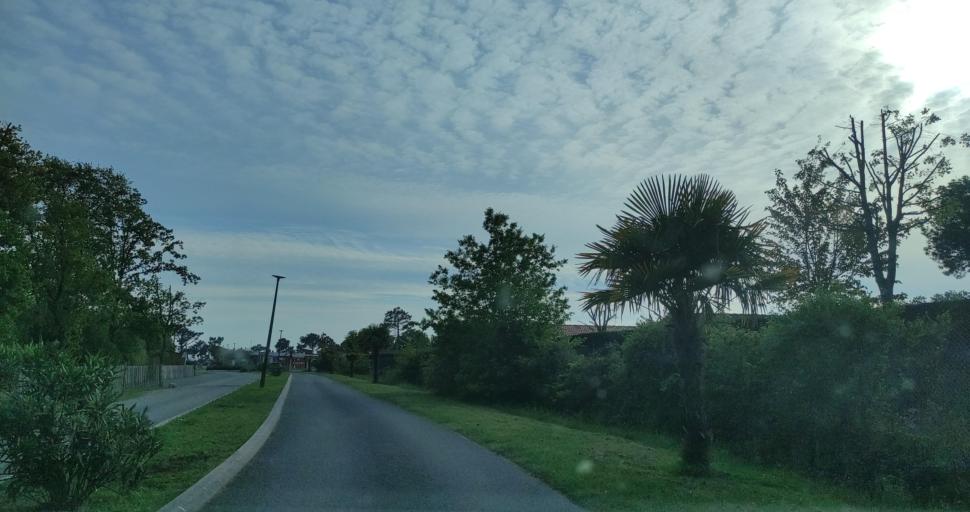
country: FR
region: Aquitaine
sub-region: Departement de la Gironde
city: Lanton
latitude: 44.7056
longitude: -1.0472
